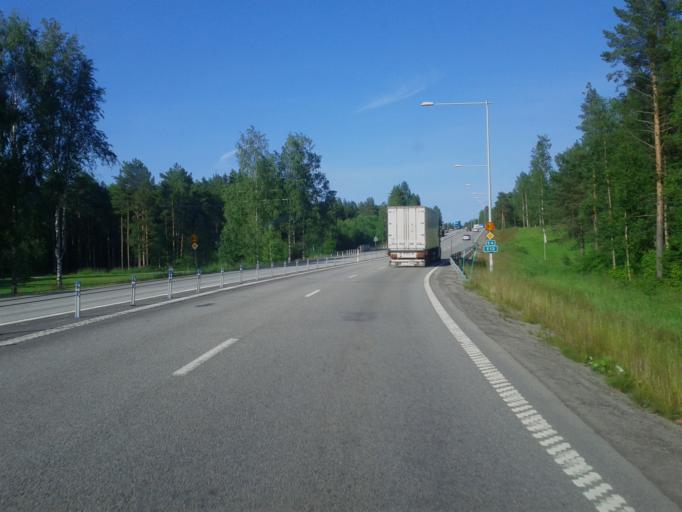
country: SE
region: Vaesterbotten
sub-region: Umea Kommun
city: Umea
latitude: 63.8027
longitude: 20.3120
